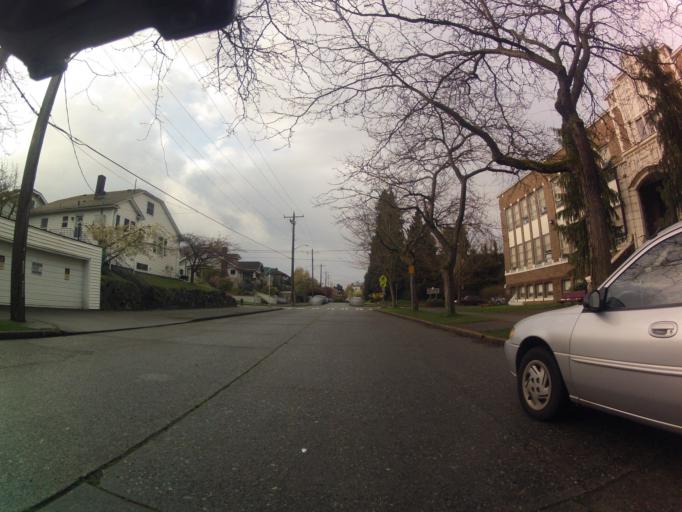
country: US
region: Washington
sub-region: King County
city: Seattle
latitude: 47.6640
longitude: -122.3364
